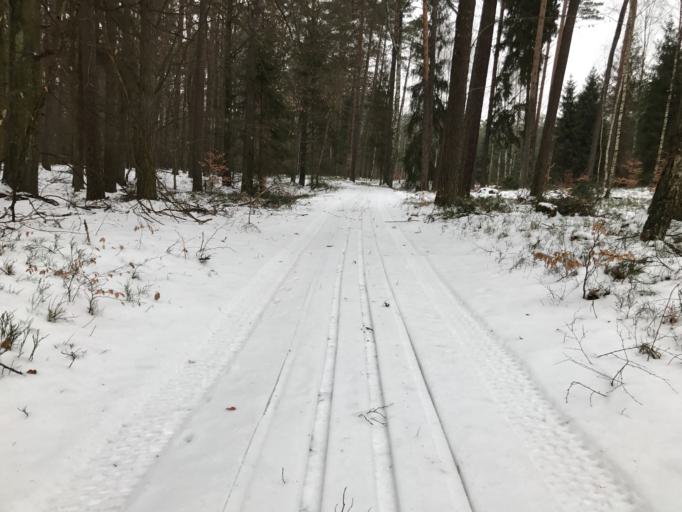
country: PL
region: Kujawsko-Pomorskie
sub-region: Powiat brodnicki
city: Gorzno
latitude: 53.1873
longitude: 19.6933
